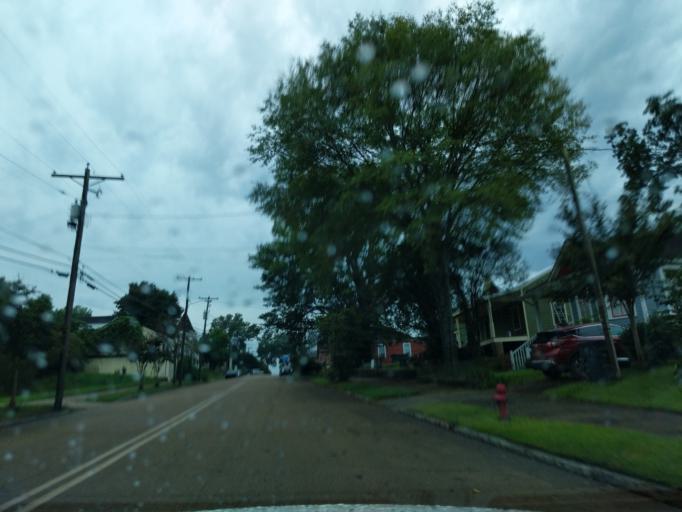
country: US
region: Mississippi
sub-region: Warren County
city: Vicksburg
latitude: 32.3560
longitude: -90.8775
